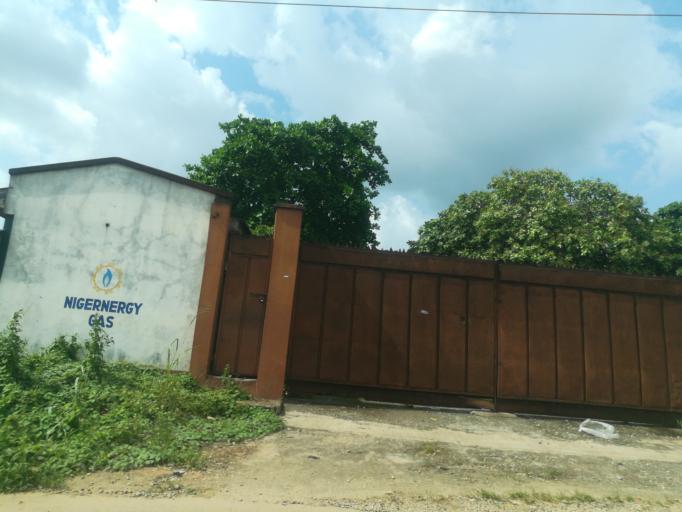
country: NG
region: Oyo
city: Ibadan
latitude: 7.3609
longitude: 3.8534
